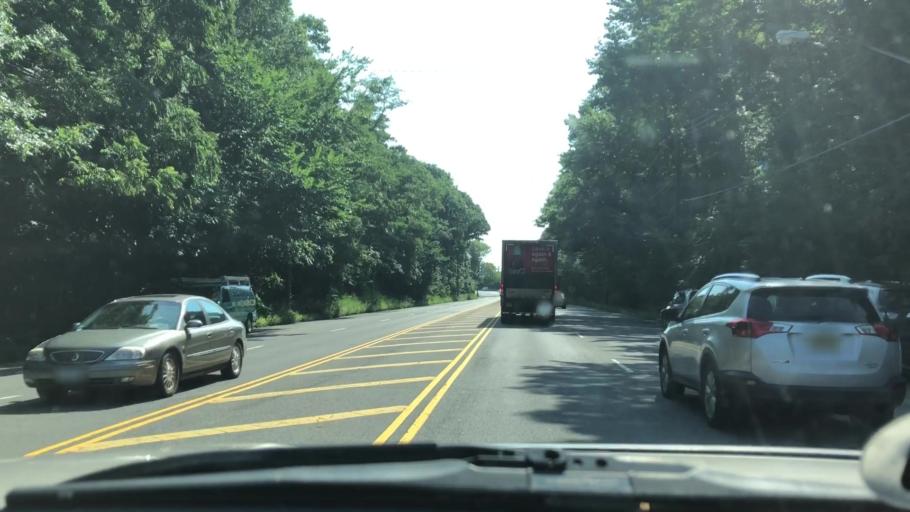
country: US
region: New York
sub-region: Richmond County
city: Staten Island
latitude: 40.5267
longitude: -74.1725
